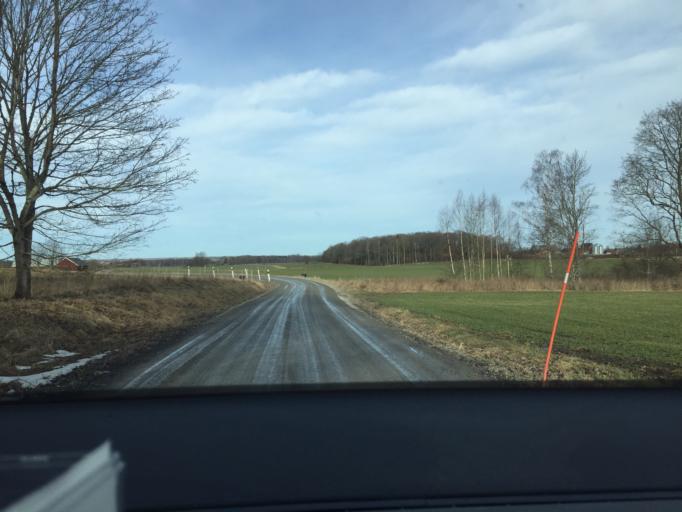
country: SE
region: OErebro
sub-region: Hallsbergs Kommun
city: Skollersta
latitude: 59.1415
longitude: 15.4161
